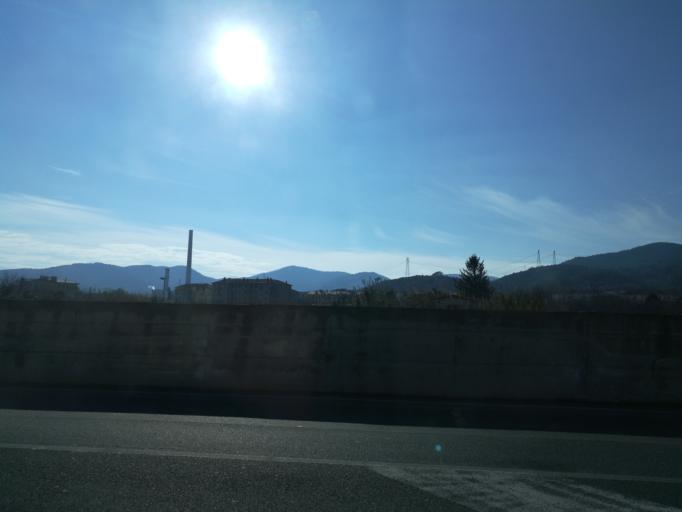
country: IT
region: Liguria
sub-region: Provincia di Savona
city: Valleggia
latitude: 44.2874
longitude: 8.4305
